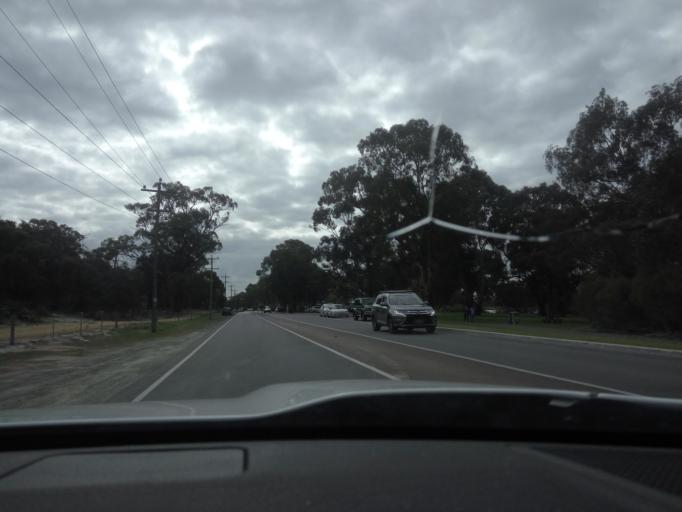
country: AU
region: Western Australia
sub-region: City of Cockburn
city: Bibra Lake
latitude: -32.0893
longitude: 115.8209
